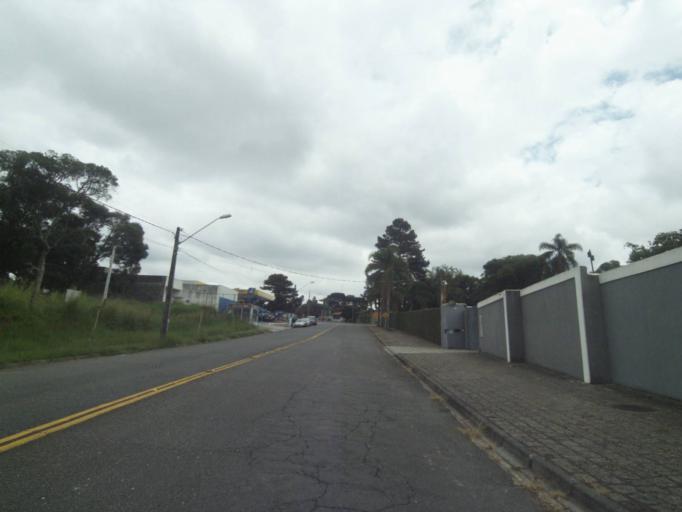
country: BR
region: Parana
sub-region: Curitiba
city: Curitiba
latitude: -25.4013
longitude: -49.2831
